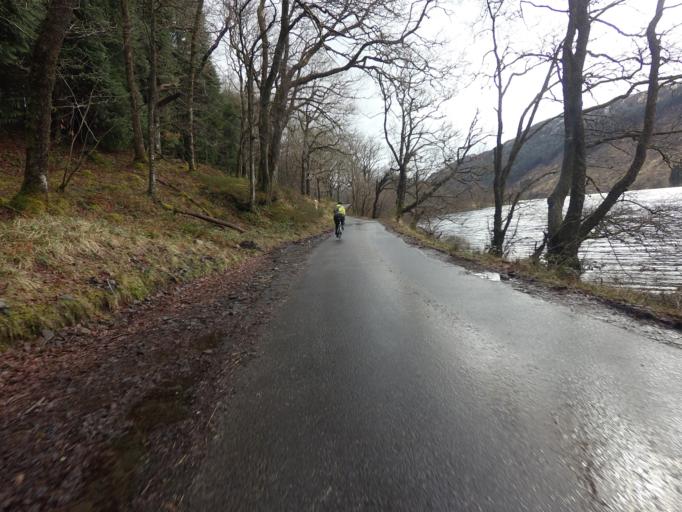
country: GB
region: Scotland
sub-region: West Dunbartonshire
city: Balloch
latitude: 56.2221
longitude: -4.5505
